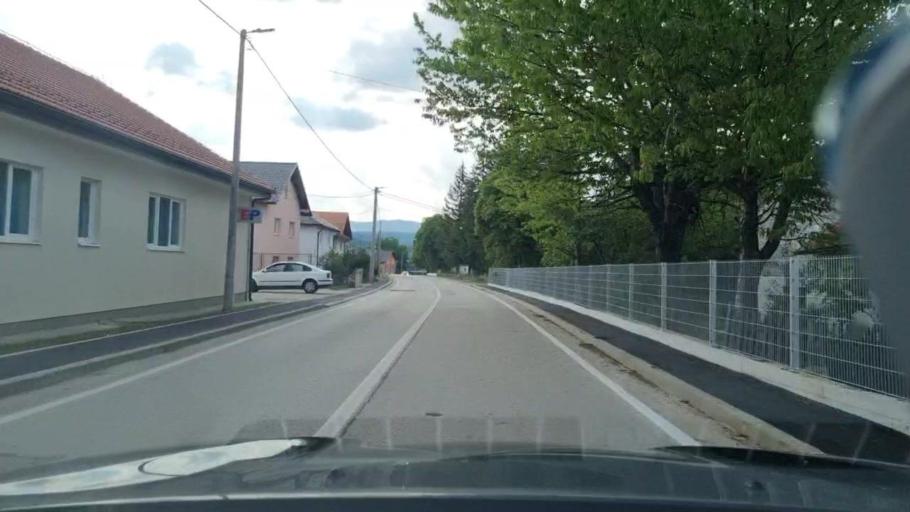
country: BA
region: Federation of Bosnia and Herzegovina
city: Glamoc
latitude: 44.0481
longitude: 16.8544
